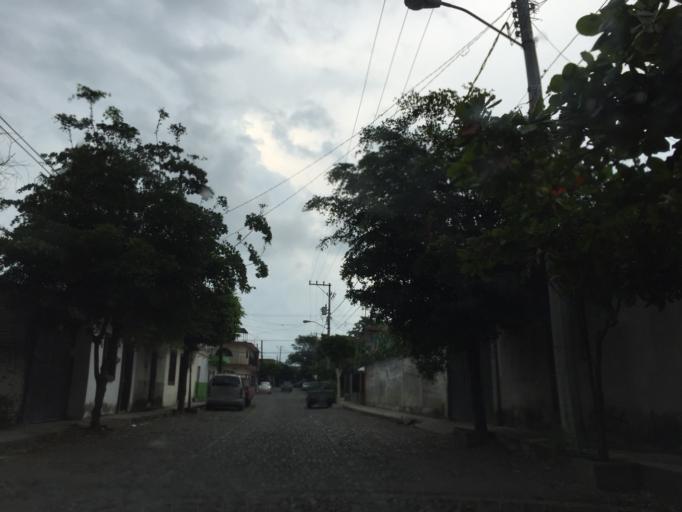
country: MX
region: Colima
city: Comala
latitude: 19.3284
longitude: -103.7588
